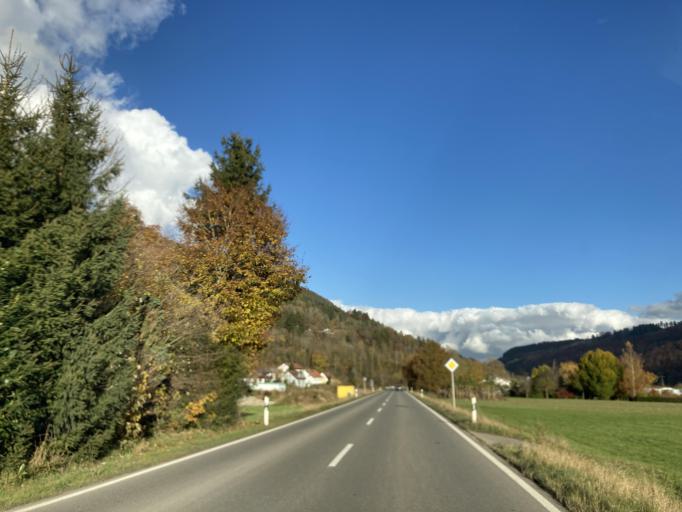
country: DE
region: Baden-Wuerttemberg
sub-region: Freiburg Region
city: Sulz am Neckar
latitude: 48.3727
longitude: 8.5811
